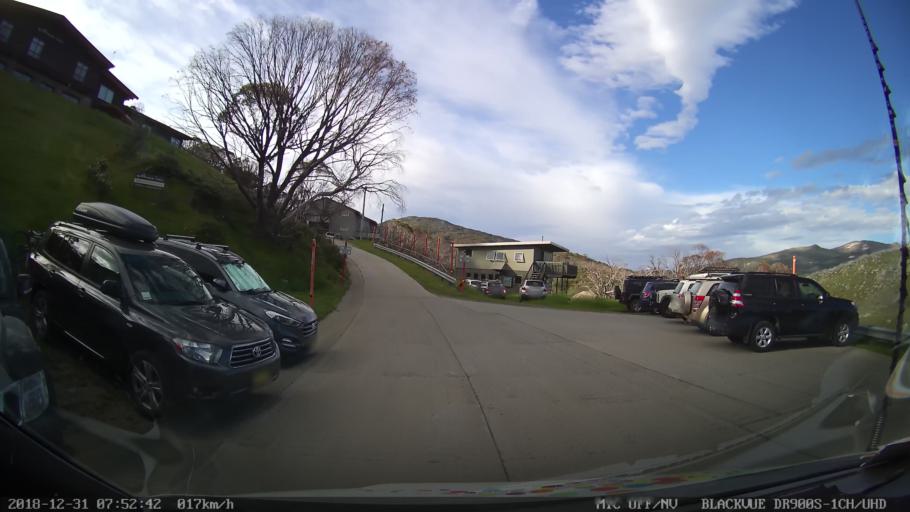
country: AU
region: New South Wales
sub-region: Snowy River
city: Jindabyne
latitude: -36.3819
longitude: 148.3727
